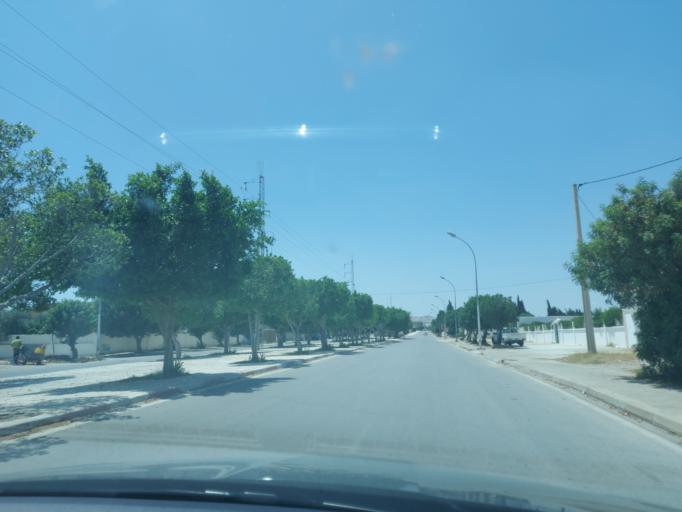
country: TN
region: Silyanah
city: Siliana
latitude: 36.0850
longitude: 9.3631
